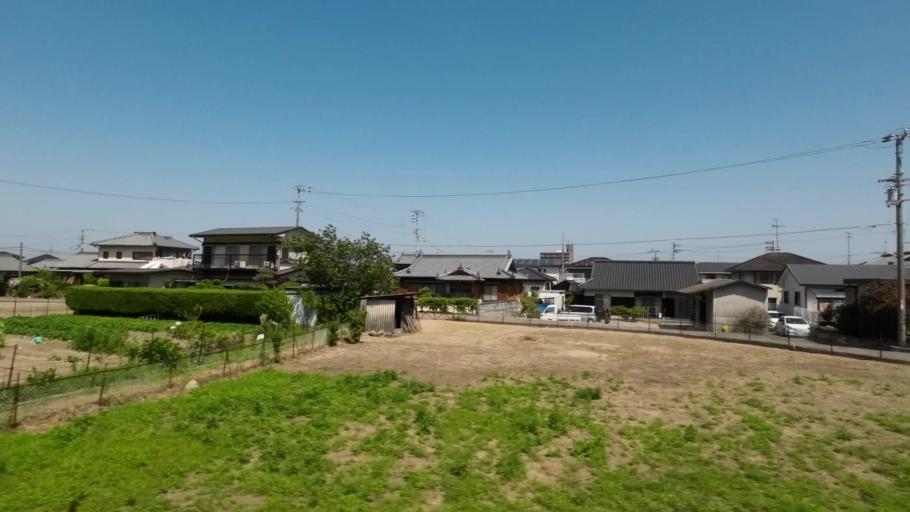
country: JP
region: Ehime
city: Niihama
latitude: 33.9629
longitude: 133.3128
